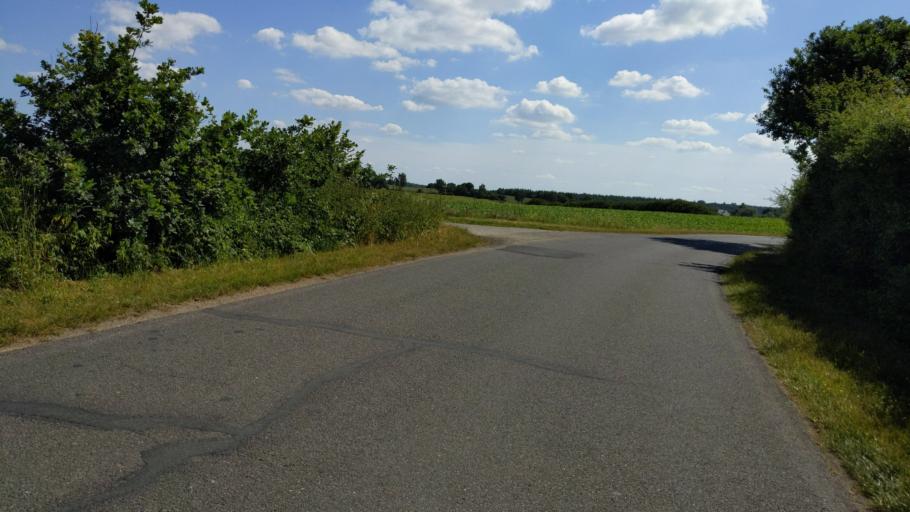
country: DE
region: Schleswig-Holstein
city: Harmsdorf
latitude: 53.6940
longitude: 10.7202
